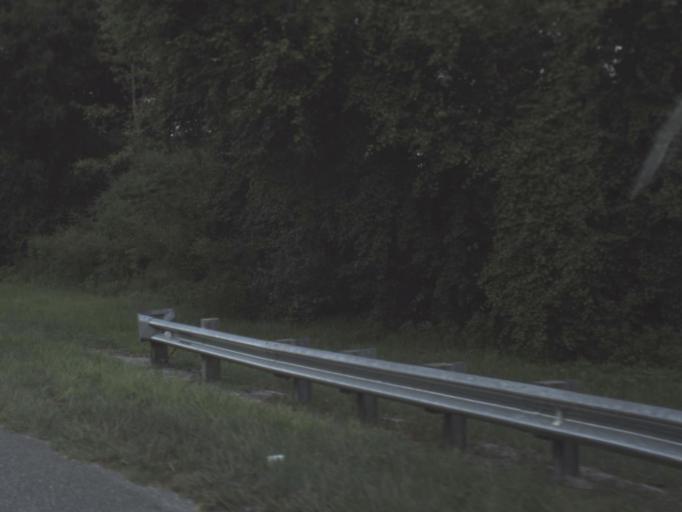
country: US
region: Florida
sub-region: Hernando County
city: North Brooksville
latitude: 28.6076
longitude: -82.3605
